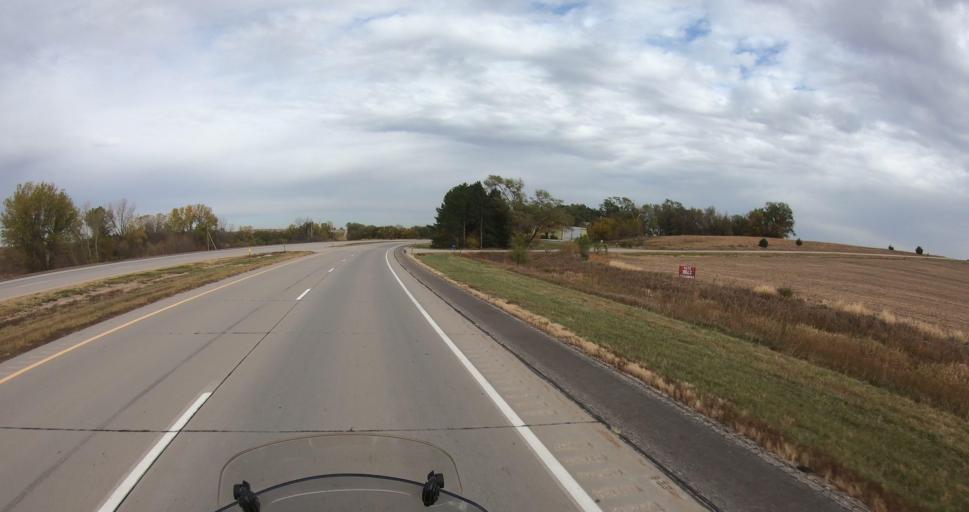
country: US
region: Nebraska
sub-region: Saunders County
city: Wahoo
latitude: 41.0923
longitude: -96.6398
